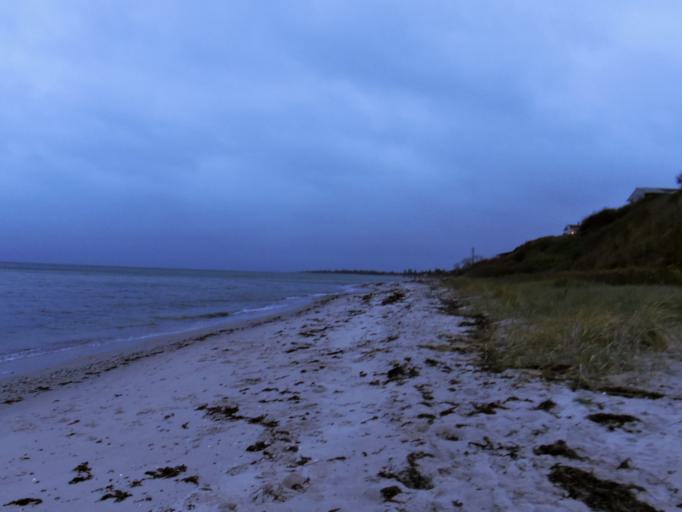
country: DK
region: Central Jutland
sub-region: Arhus Kommune
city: Malling
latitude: 55.9889
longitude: 10.2527
